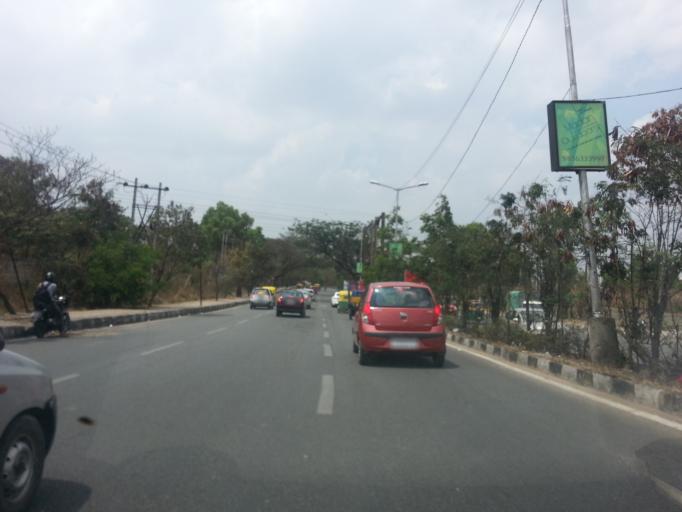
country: IN
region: Karnataka
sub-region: Bangalore Urban
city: Bangalore
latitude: 12.9483
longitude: 77.6405
